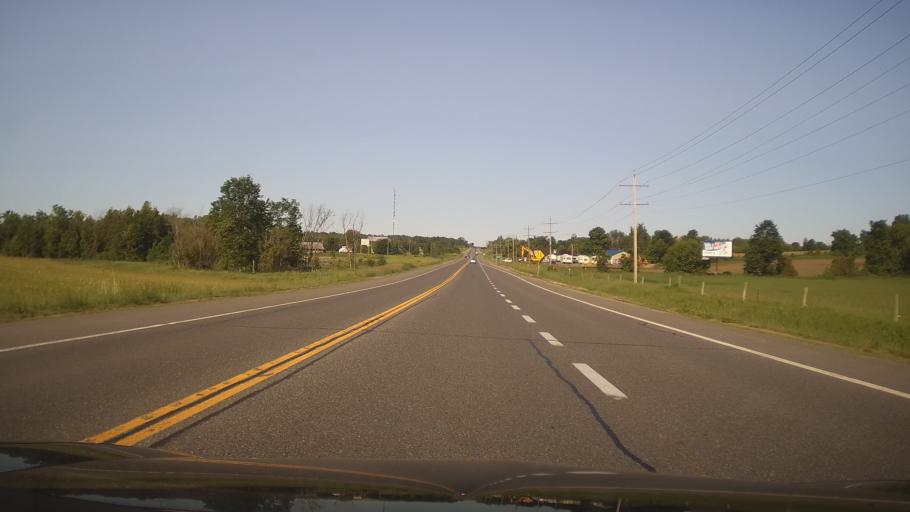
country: CA
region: Ontario
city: Peterborough
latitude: 44.3597
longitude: -78.0285
